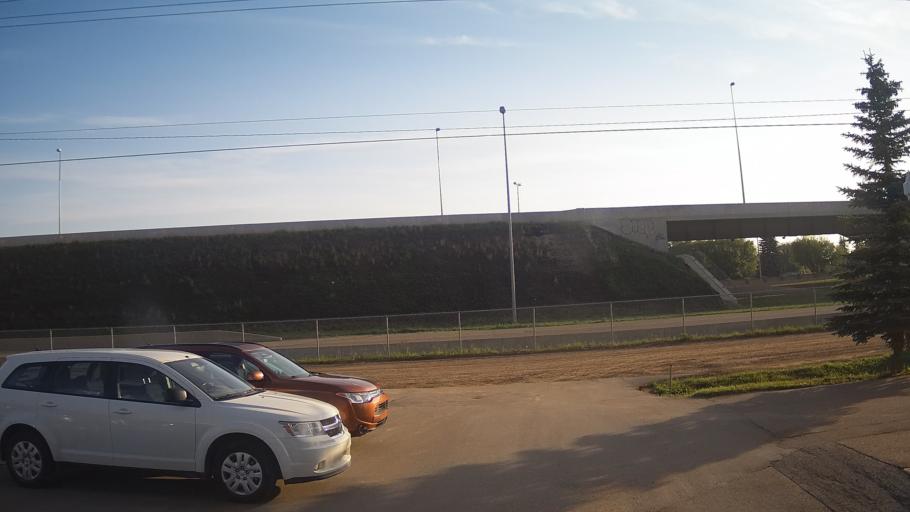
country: CA
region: Saskatchewan
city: Saskatoon
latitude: 52.0920
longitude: -106.6638
